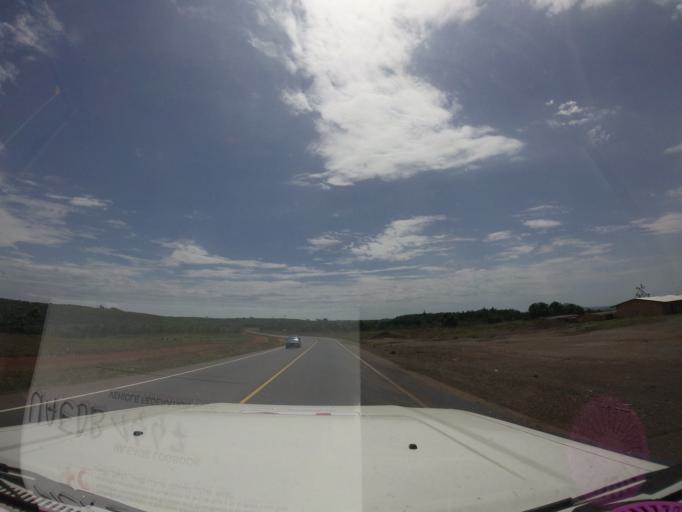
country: LR
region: Margibi
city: Kakata
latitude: 6.4491
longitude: -10.4414
